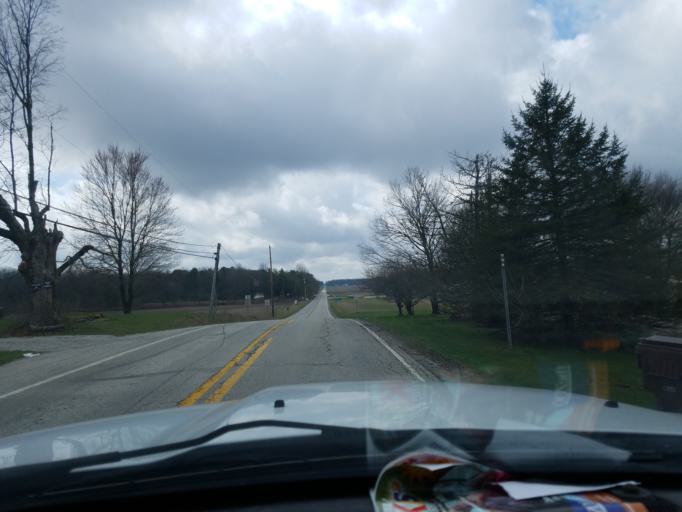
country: US
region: Indiana
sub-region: Vigo County
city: Seelyville
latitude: 39.3890
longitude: -87.3051
